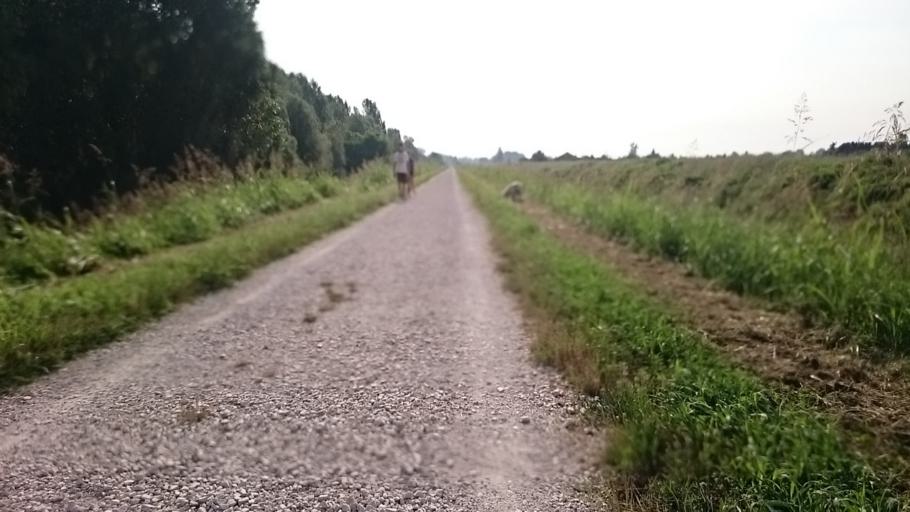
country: IT
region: Veneto
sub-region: Provincia di Venezia
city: Tombelle
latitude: 45.4081
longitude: 11.9811
